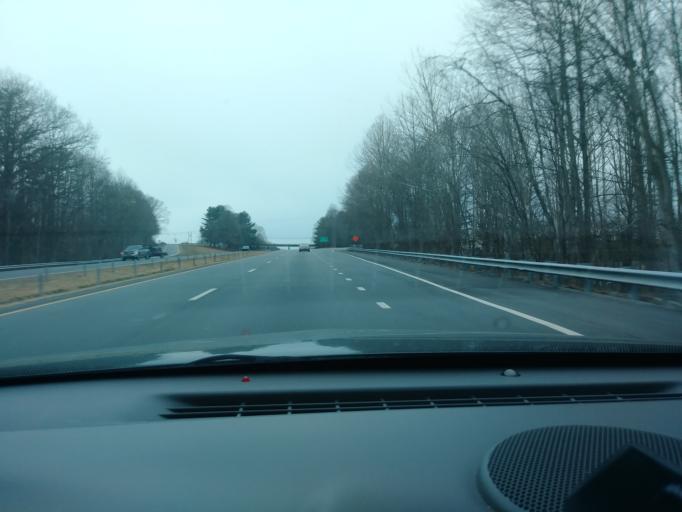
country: US
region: North Carolina
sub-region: Wilkes County
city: Wilkesboro
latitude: 36.1338
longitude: -81.1421
